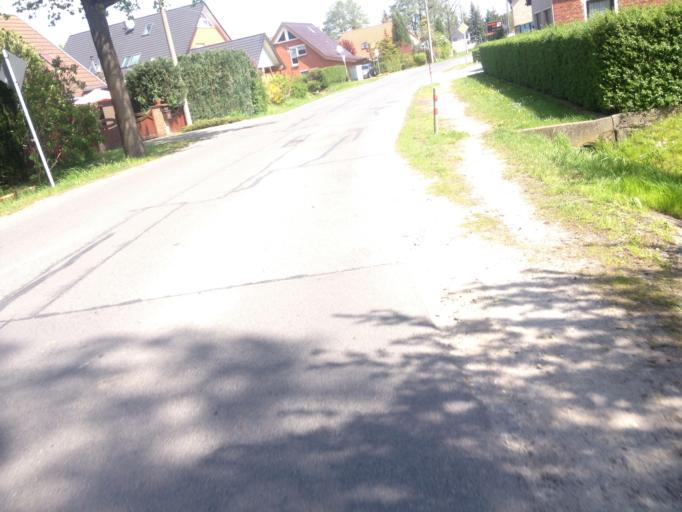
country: DE
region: Brandenburg
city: Drehnow
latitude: 51.8233
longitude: 14.3401
